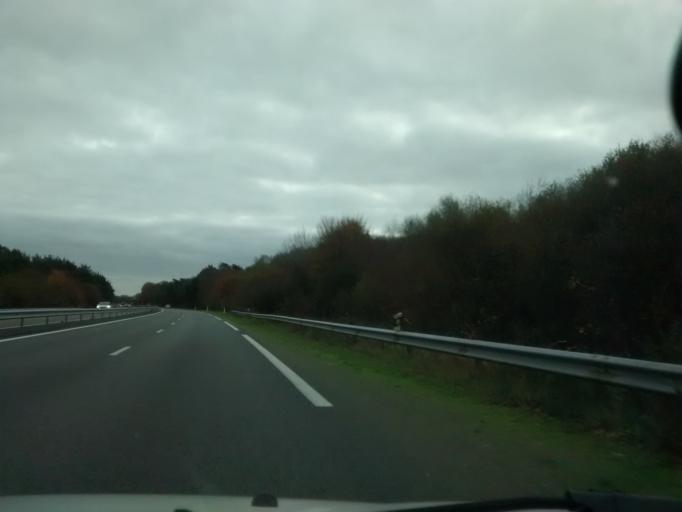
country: FR
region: Brittany
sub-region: Departement d'Ille-et-Vilaine
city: Saint-Pierre-de-Plesguen
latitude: 48.4357
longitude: -1.9218
